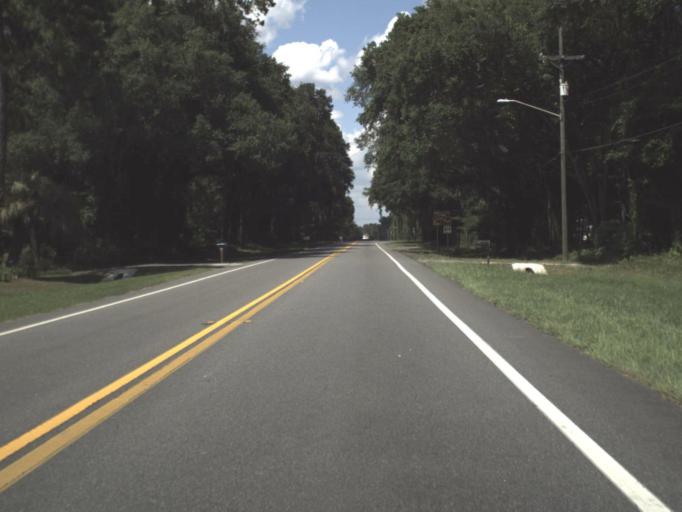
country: US
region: Florida
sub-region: Alachua County
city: Gainesville
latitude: 29.6755
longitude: -82.2542
